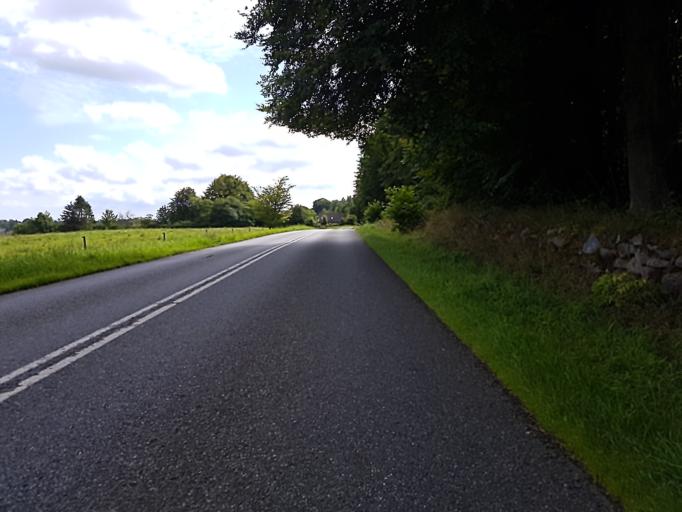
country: DK
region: Capital Region
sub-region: Fureso Kommune
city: Farum
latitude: 55.8117
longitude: 12.3201
